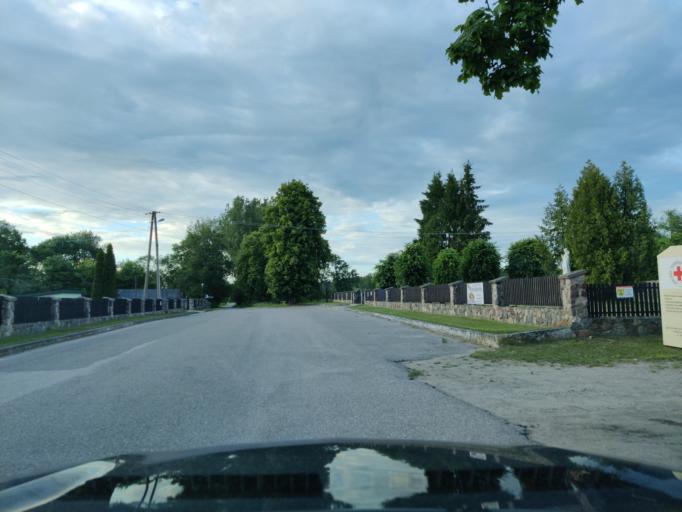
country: PL
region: Masovian Voivodeship
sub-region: Powiat pultuski
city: Obryte
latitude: 52.7571
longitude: 21.2170
